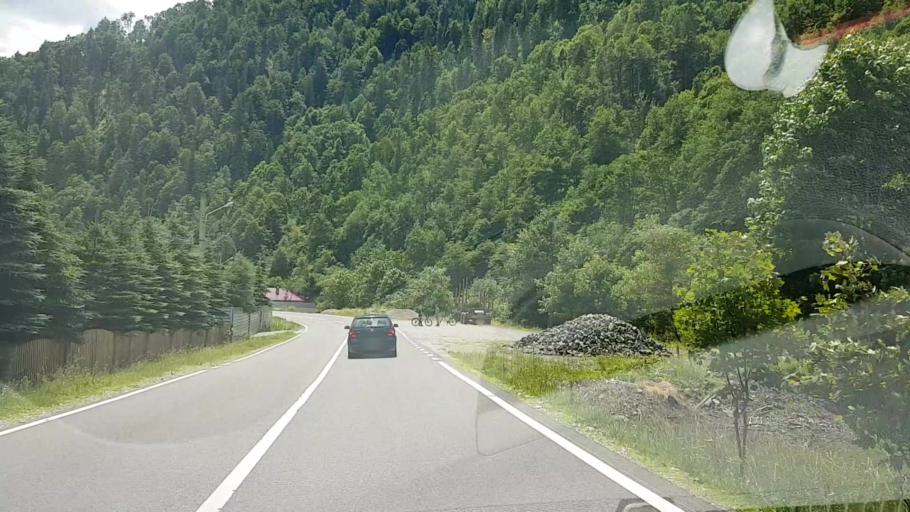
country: RO
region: Suceava
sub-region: Comuna Brosteni
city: Brosteni
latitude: 47.2753
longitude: 25.6480
